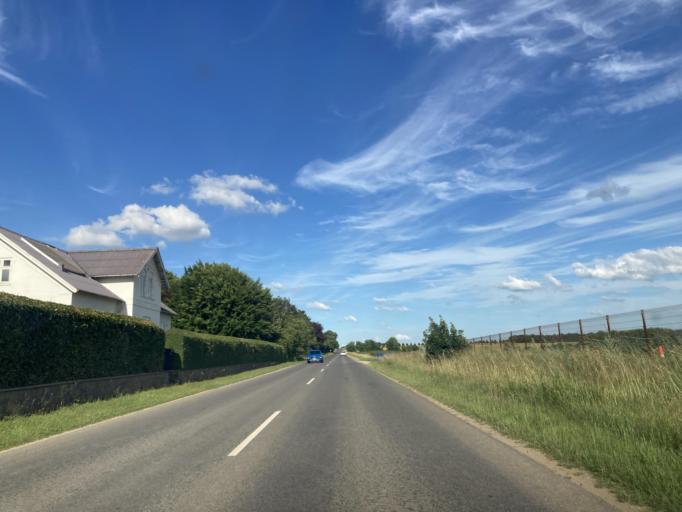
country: DK
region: South Denmark
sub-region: Kolding Kommune
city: Lunderskov
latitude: 55.4852
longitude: 9.3310
